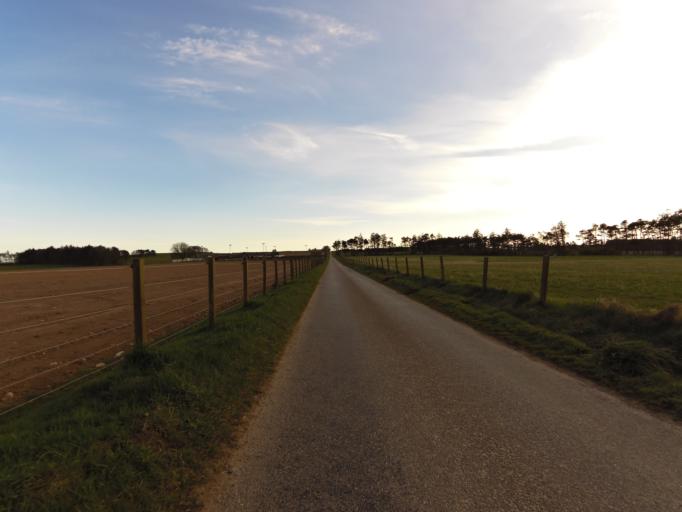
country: GB
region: Scotland
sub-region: Aberdeenshire
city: Stonehaven
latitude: 56.9454
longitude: -2.2196
